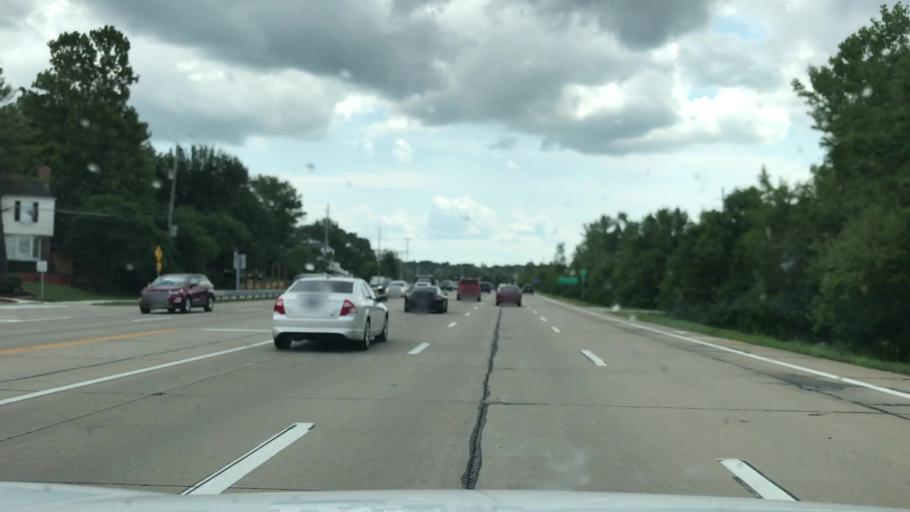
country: US
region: Missouri
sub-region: Saint Charles County
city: Dardenne Prairie
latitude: 38.7491
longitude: -90.7000
